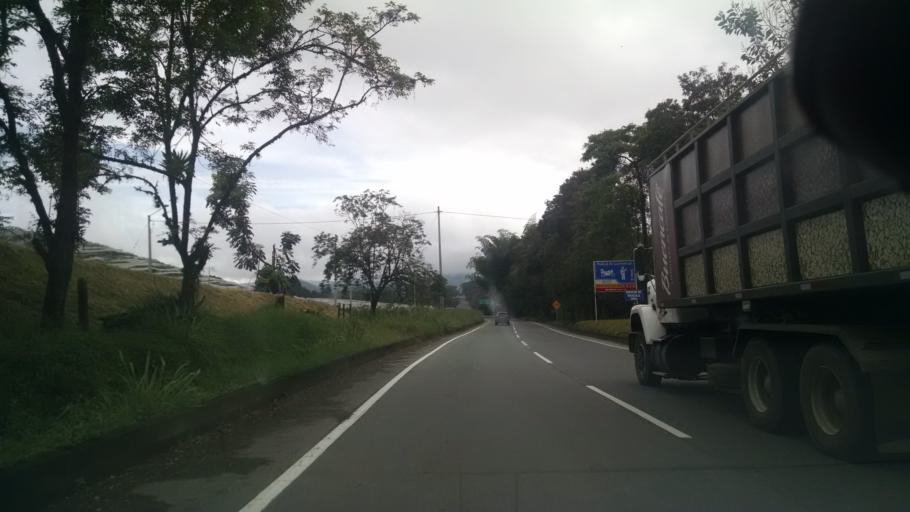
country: CO
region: Caldas
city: Chinchina
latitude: 5.0052
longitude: -75.5957
